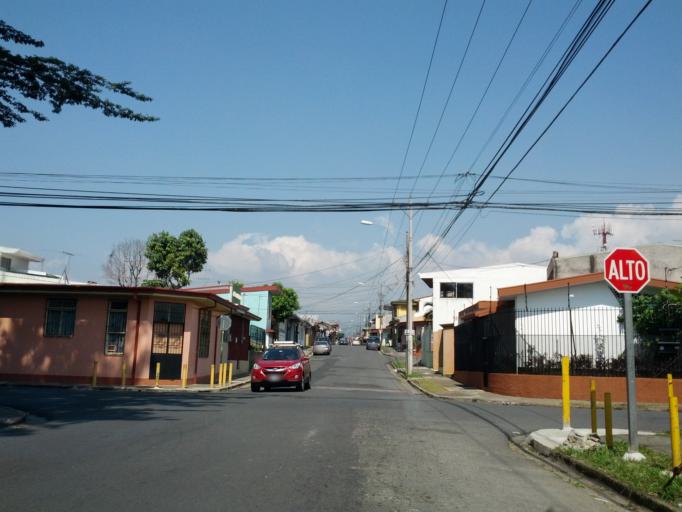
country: CR
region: Alajuela
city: Alajuela
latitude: 10.0149
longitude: -84.2075
